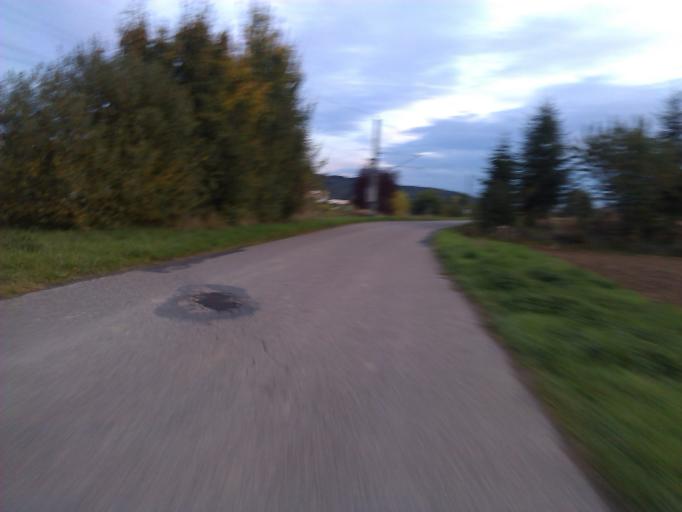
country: DE
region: Baden-Wuerttemberg
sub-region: Karlsruhe Region
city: Zuzenhausen
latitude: 49.3062
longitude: 8.8142
